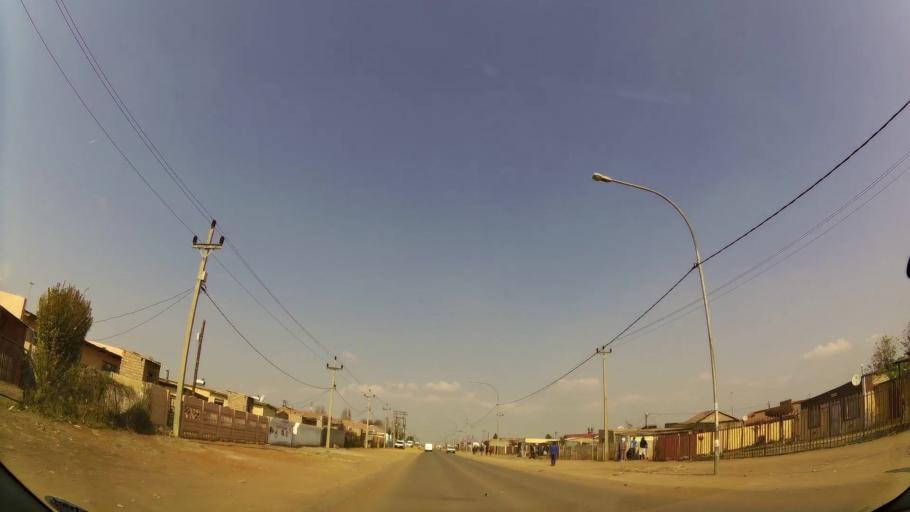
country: ZA
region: Gauteng
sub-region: Ekurhuleni Metropolitan Municipality
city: Springs
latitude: -26.1143
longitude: 28.4752
